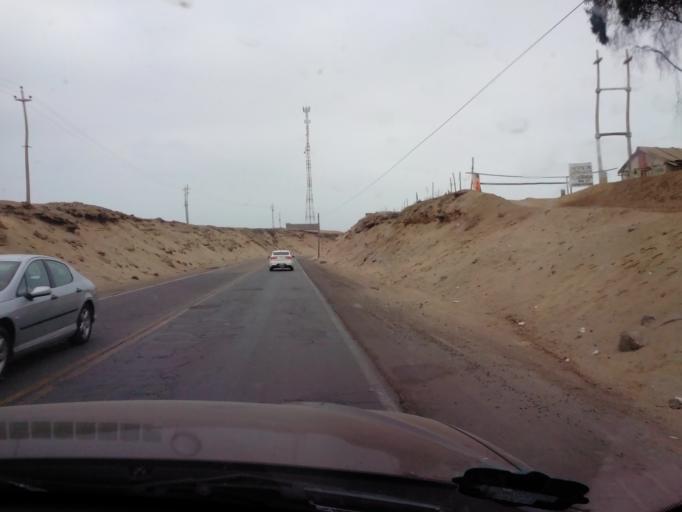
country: PE
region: Ica
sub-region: Provincia de Chincha
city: Sunampe
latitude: -13.4137
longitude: -76.1845
